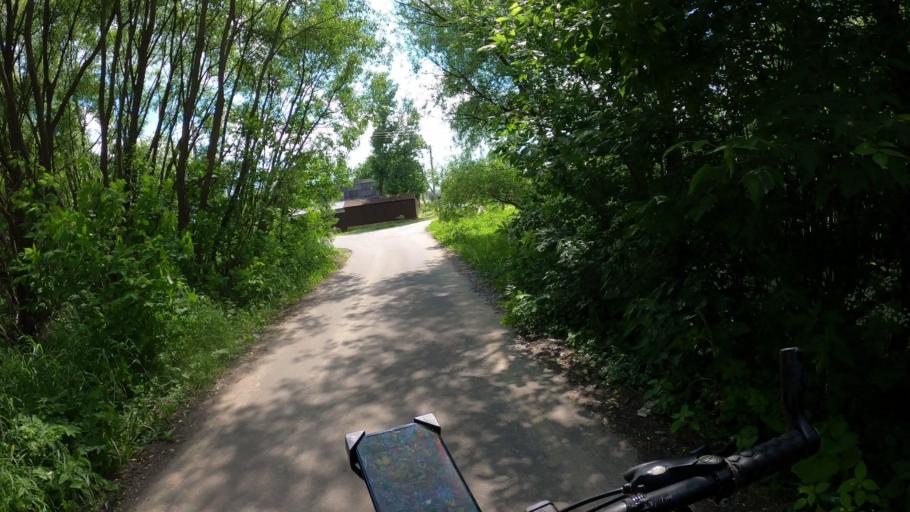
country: RU
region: Moskovskaya
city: Konobeyevo
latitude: 55.3967
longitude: 38.6786
